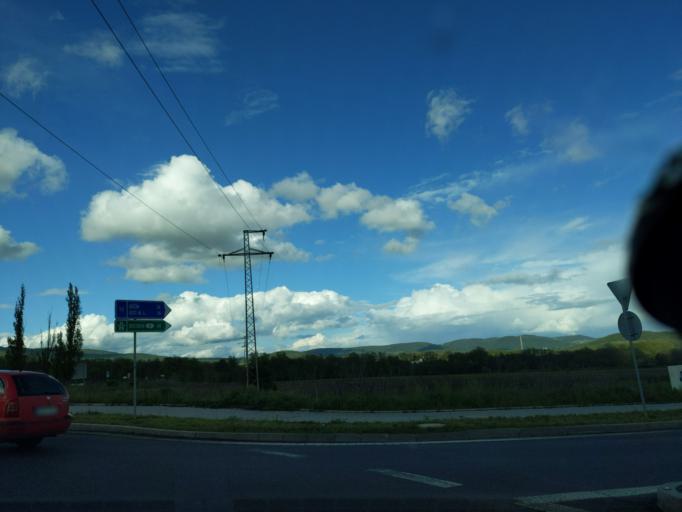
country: CZ
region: Ustecky
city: Chlumec
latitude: 50.6853
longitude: 13.9214
